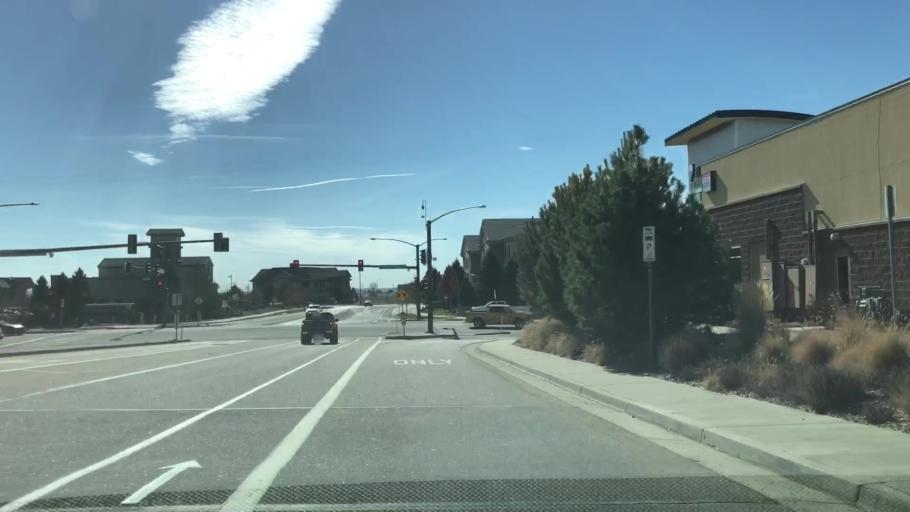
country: US
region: Colorado
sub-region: Larimer County
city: Loveland
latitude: 40.4367
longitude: -104.9881
